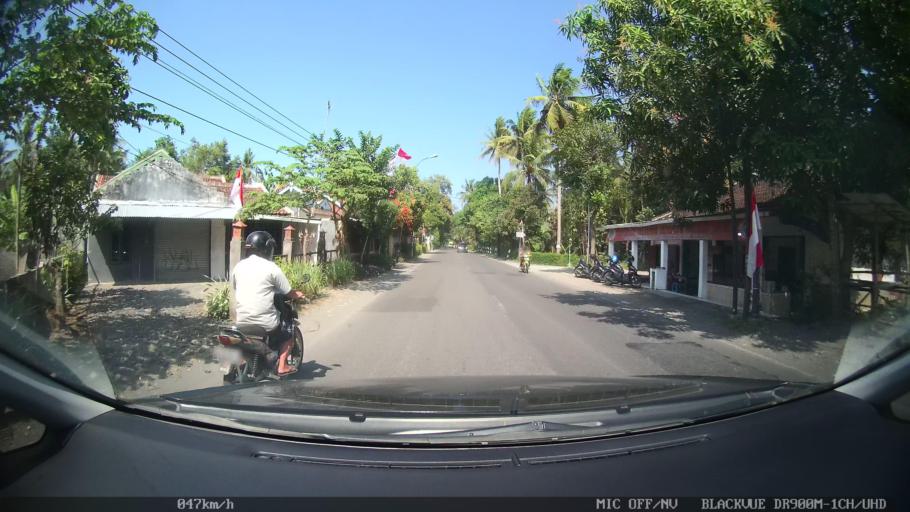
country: ID
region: Daerah Istimewa Yogyakarta
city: Srandakan
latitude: -7.9417
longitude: 110.2320
